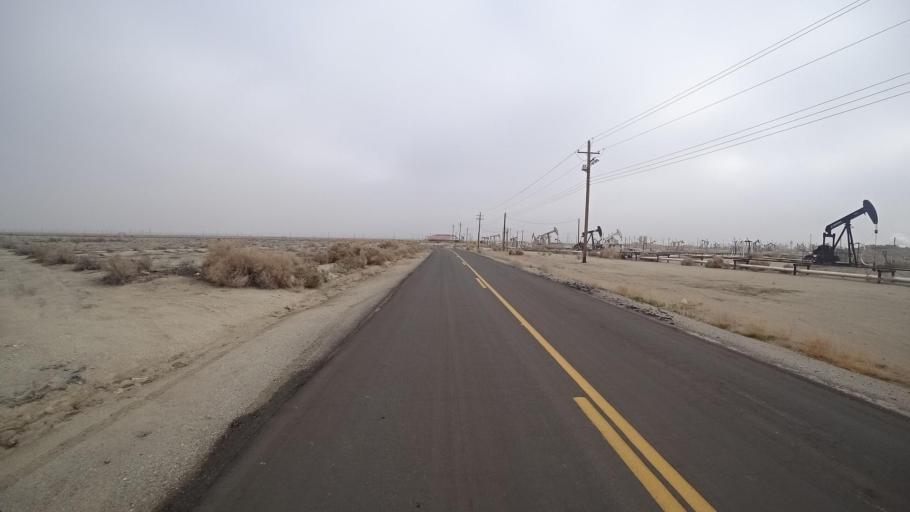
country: US
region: California
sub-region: Kern County
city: Maricopa
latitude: 35.0836
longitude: -119.3896
